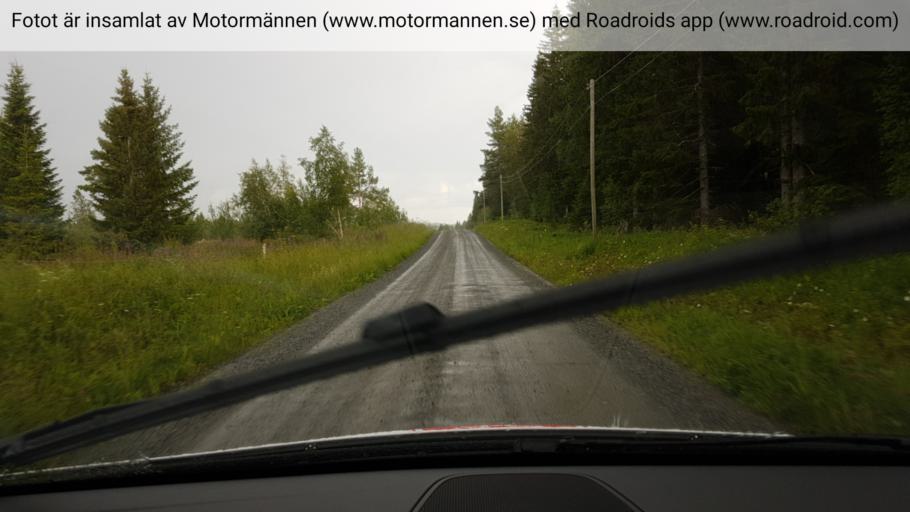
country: SE
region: Jaemtland
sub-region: OEstersunds Kommun
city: Brunflo
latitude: 63.0484
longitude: 14.6987
